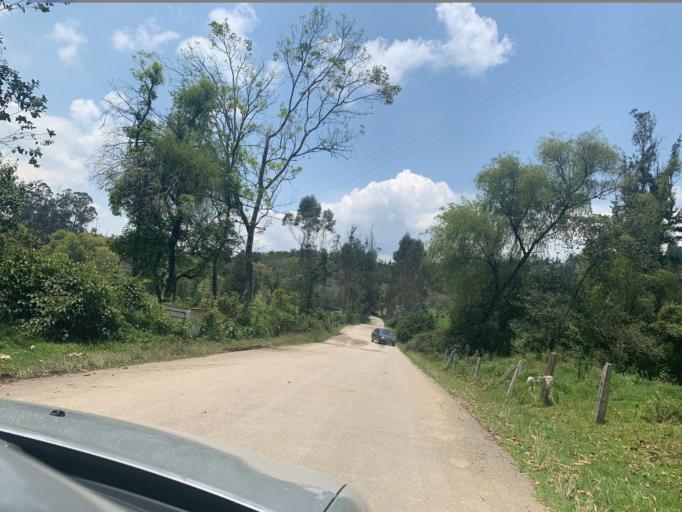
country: CO
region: Boyaca
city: Chiquinquira
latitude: 5.5743
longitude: -73.7460
